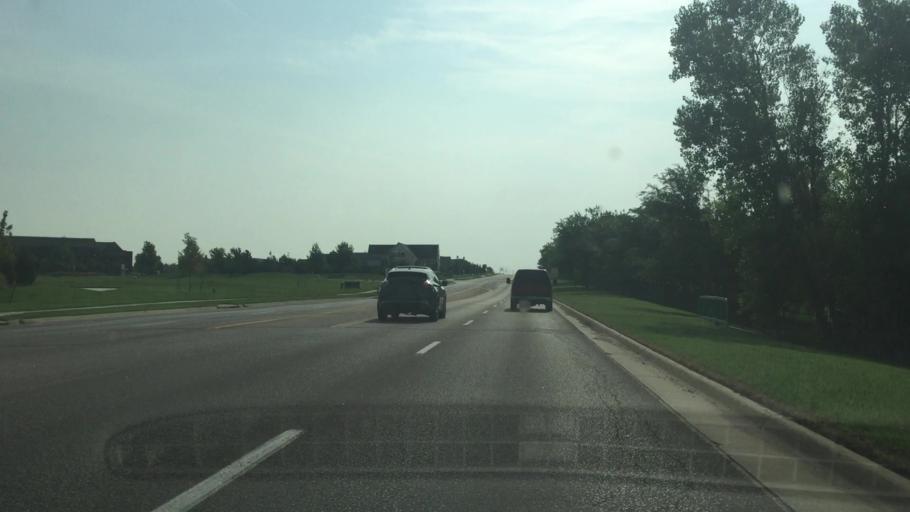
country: US
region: Kansas
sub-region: Sedgwick County
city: Bellaire
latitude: 37.7084
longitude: -97.2185
